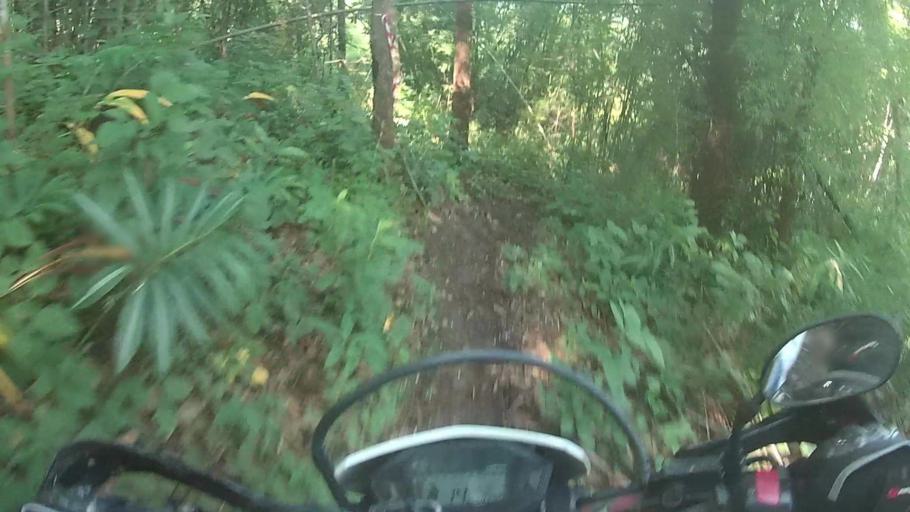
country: TH
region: Chiang Mai
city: Mae Taeng
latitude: 18.9923
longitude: 98.8585
